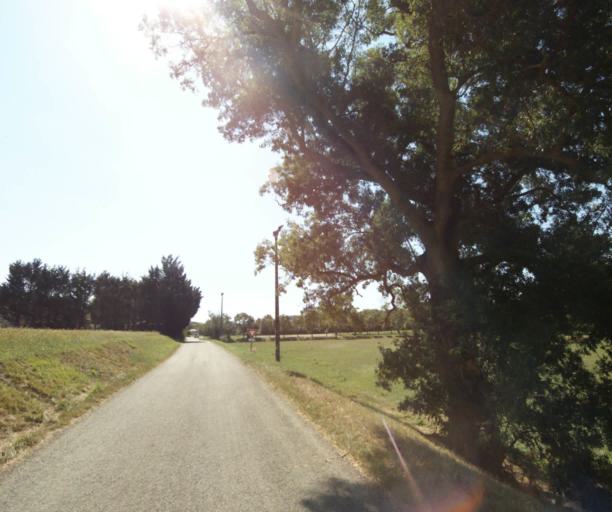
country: FR
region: Midi-Pyrenees
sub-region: Departement de l'Ariege
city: Lezat-sur-Leze
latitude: 43.2352
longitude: 1.3820
